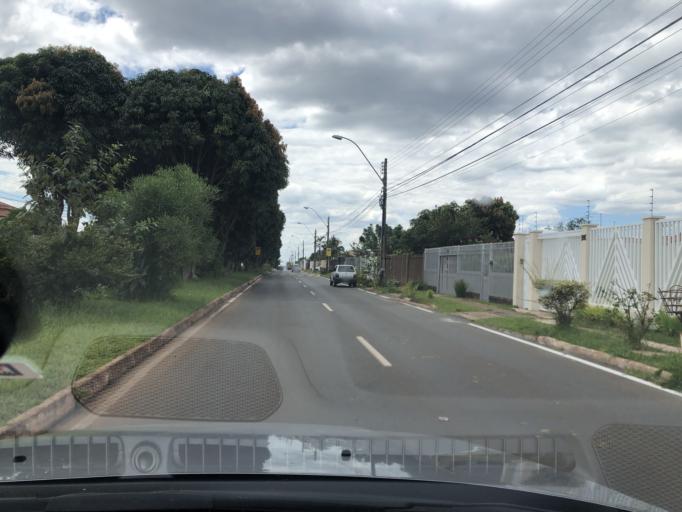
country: BR
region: Federal District
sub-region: Brasilia
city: Brasilia
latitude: -15.9945
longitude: -47.9920
